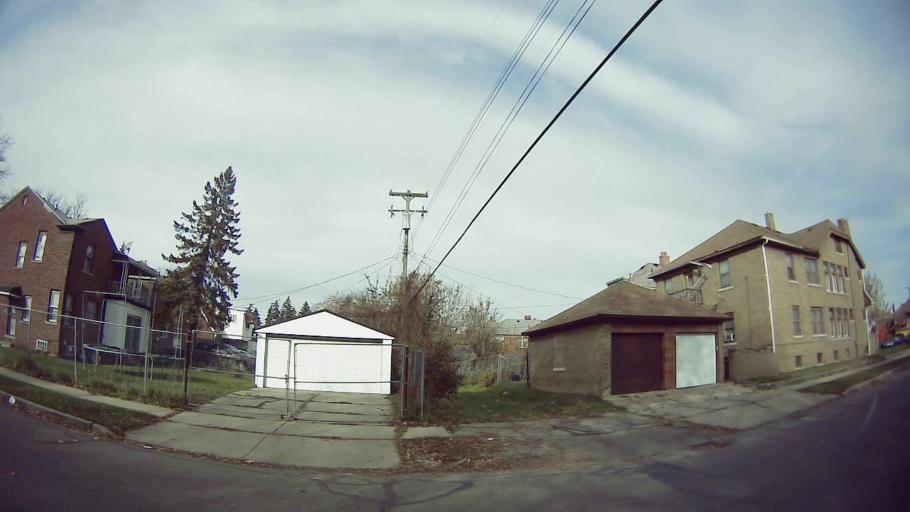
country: US
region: Michigan
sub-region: Wayne County
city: Highland Park
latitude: 42.3810
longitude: -83.1428
